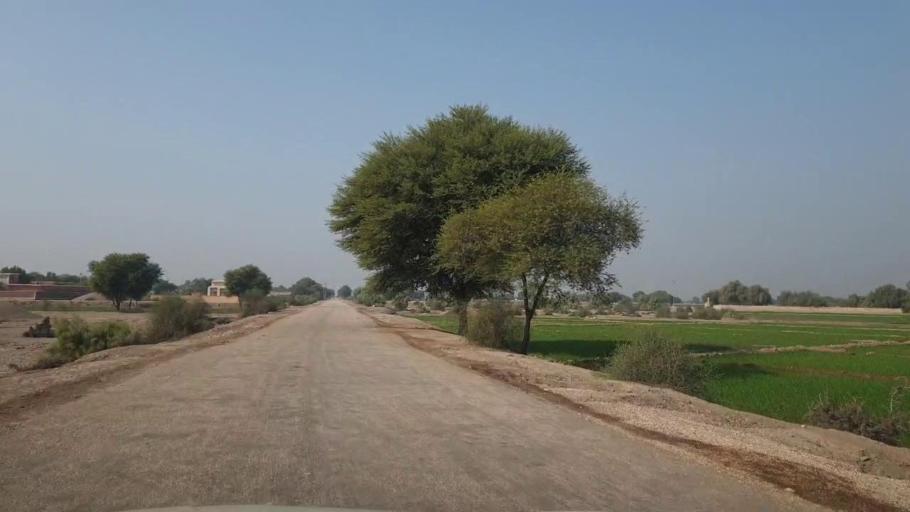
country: PK
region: Sindh
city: Bhan
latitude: 26.5078
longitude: 67.7914
